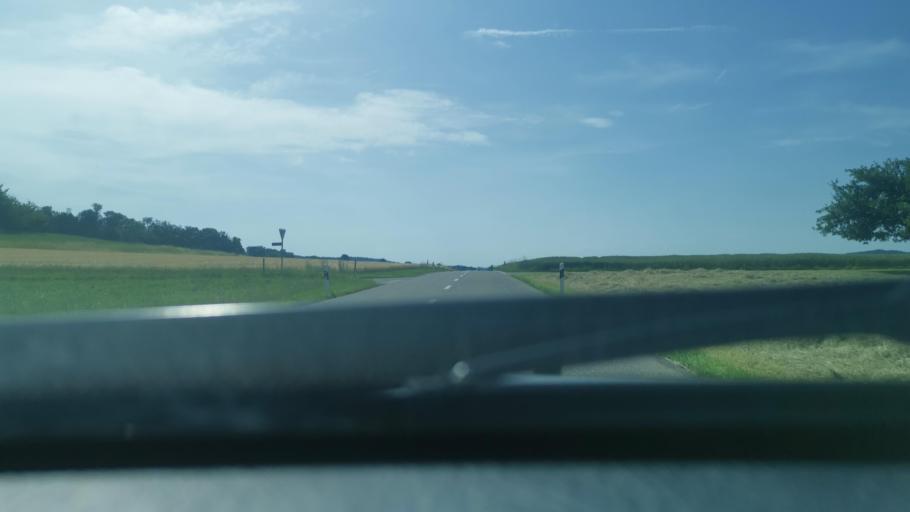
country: CH
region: Zurich
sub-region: Bezirk Winterthur
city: Sulz
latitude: 47.5692
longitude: 8.7987
